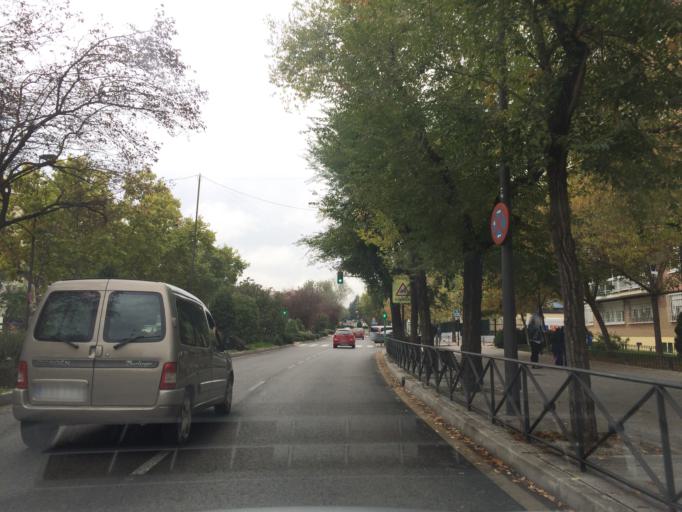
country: ES
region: Madrid
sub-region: Provincia de Madrid
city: Alcorcon
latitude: 40.3473
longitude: -3.8183
